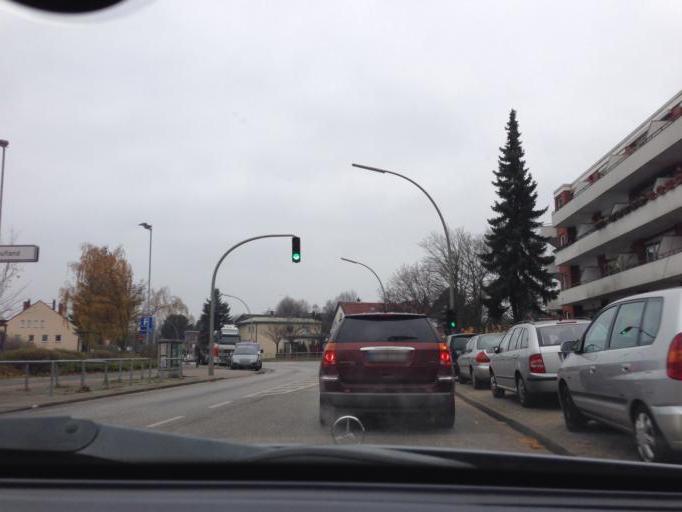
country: DE
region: Hamburg
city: Steilshoop
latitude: 53.6125
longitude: 10.0797
